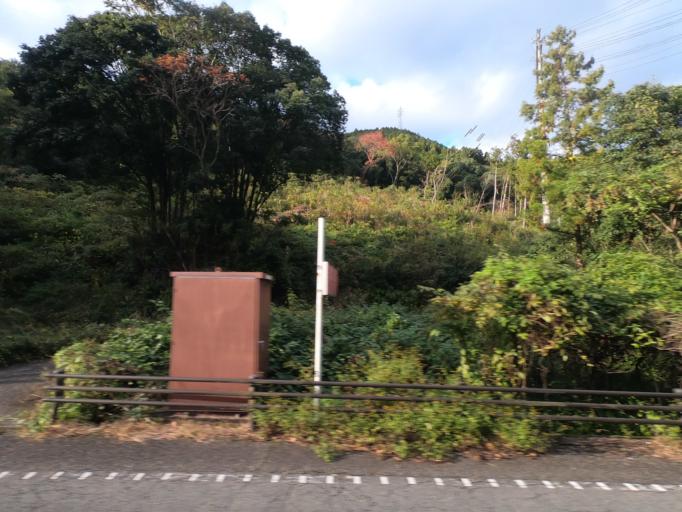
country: JP
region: Kumamoto
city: Minamata
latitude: 32.2457
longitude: 130.4862
